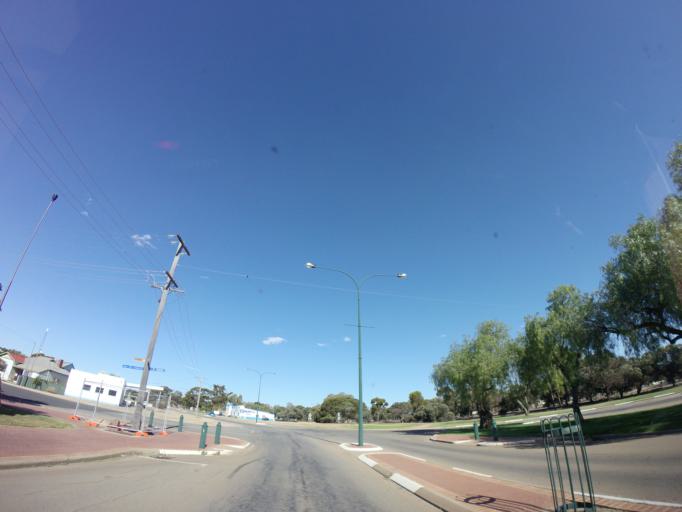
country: AU
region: Western Australia
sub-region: Merredin
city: Merredin
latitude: -31.4823
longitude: 118.2810
